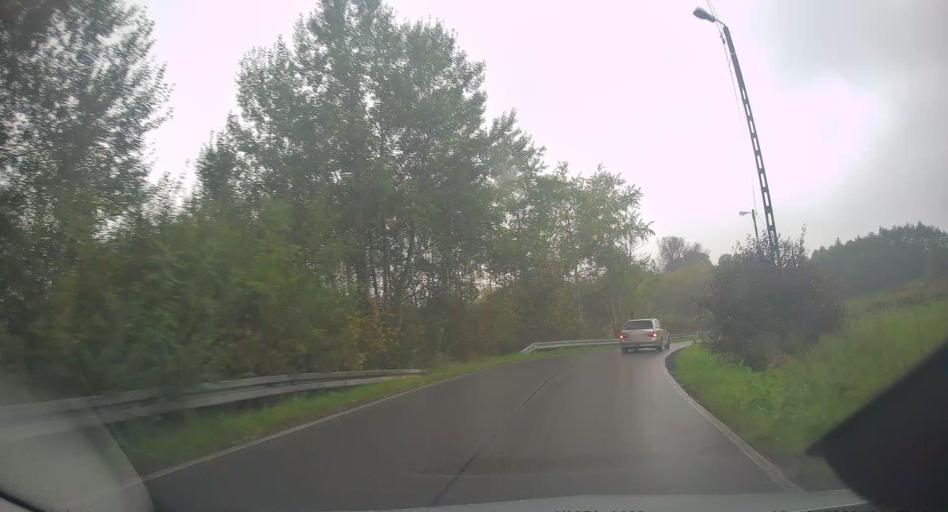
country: PL
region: Lesser Poland Voivodeship
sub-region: Powiat krakowski
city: Ochojno
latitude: 49.9630
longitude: 20.0026
